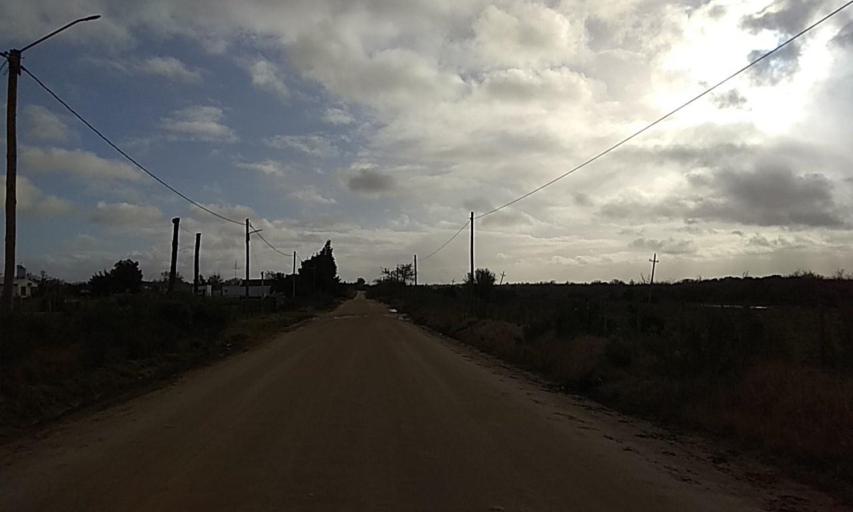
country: UY
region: Florida
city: Florida
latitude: -34.0600
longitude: -56.1919
